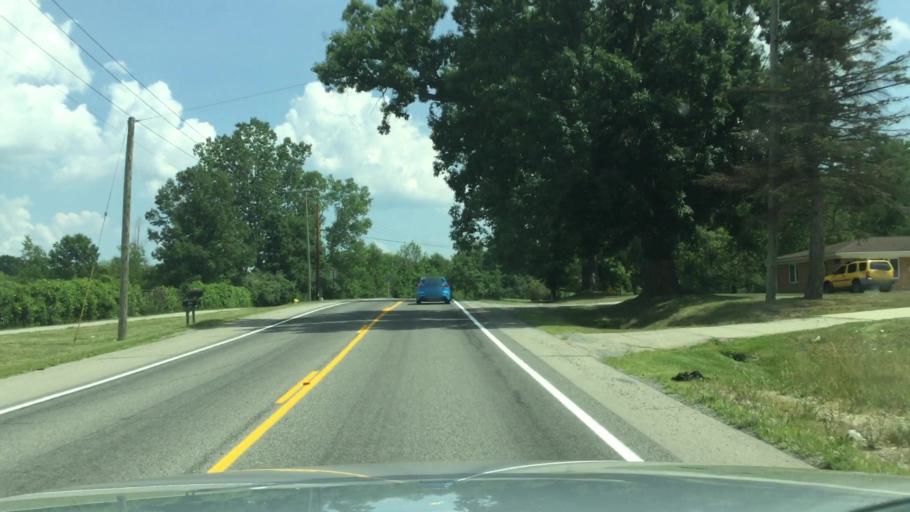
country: US
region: Michigan
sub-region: Washtenaw County
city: Ypsilanti
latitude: 42.2047
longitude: -83.6114
